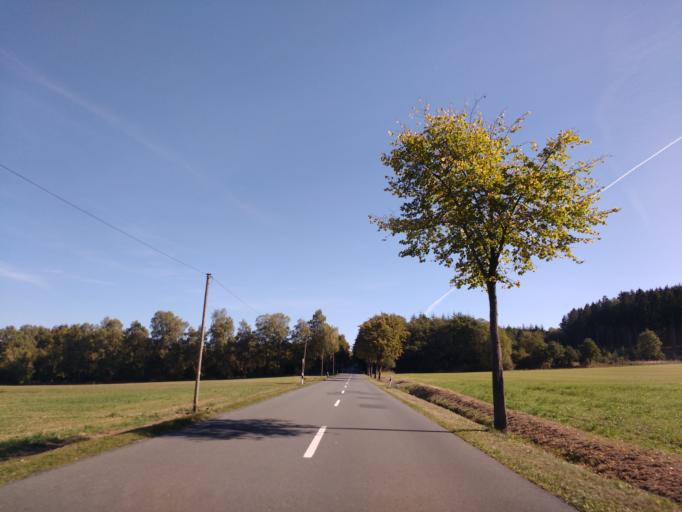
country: DE
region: North Rhine-Westphalia
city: Lichtenau
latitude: 51.6194
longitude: 8.9347
